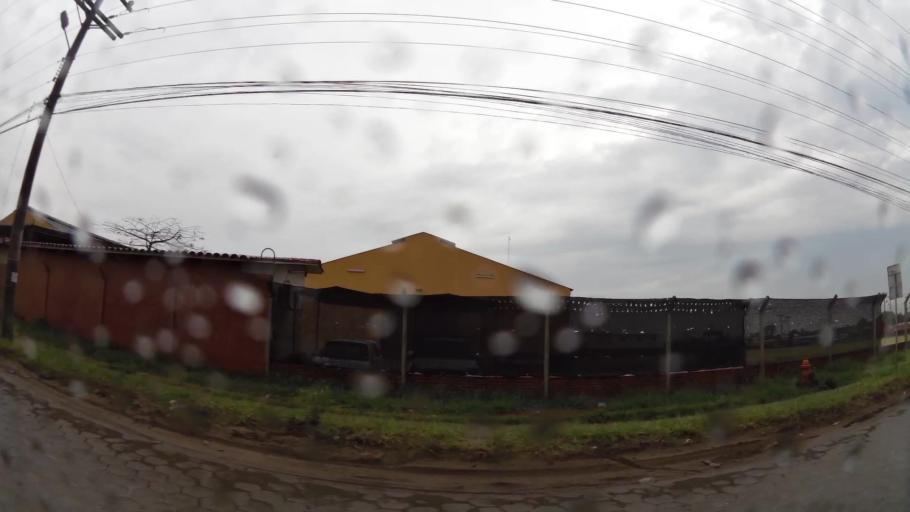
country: BO
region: Santa Cruz
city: Santa Cruz de la Sierra
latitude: -17.7560
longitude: -63.1339
